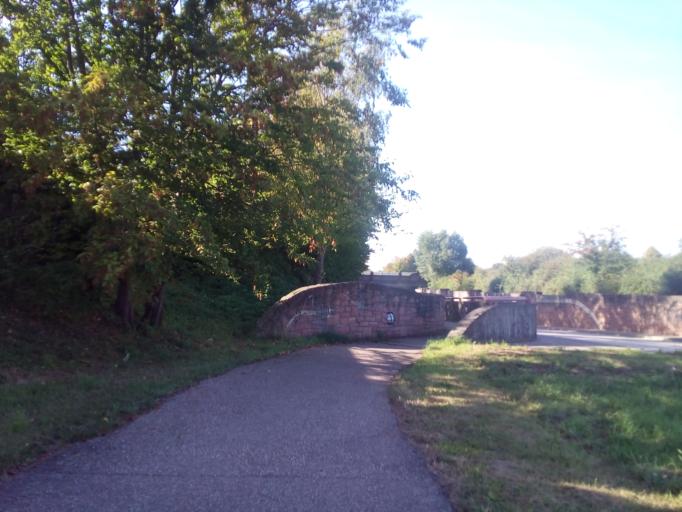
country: DE
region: Baden-Wuerttemberg
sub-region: Freiburg Region
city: Sasbach
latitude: 48.6488
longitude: 8.0850
